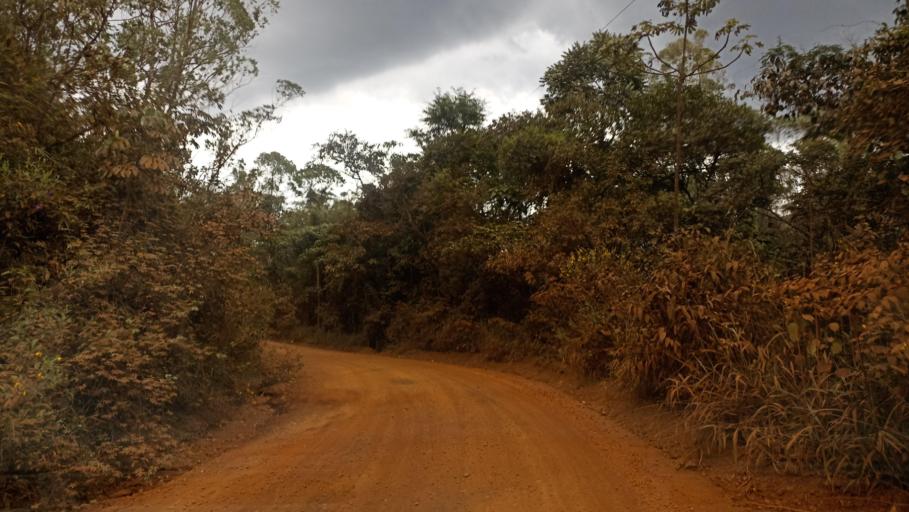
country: BR
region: Minas Gerais
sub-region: Congonhas
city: Congonhas
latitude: -20.4219
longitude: -43.7757
